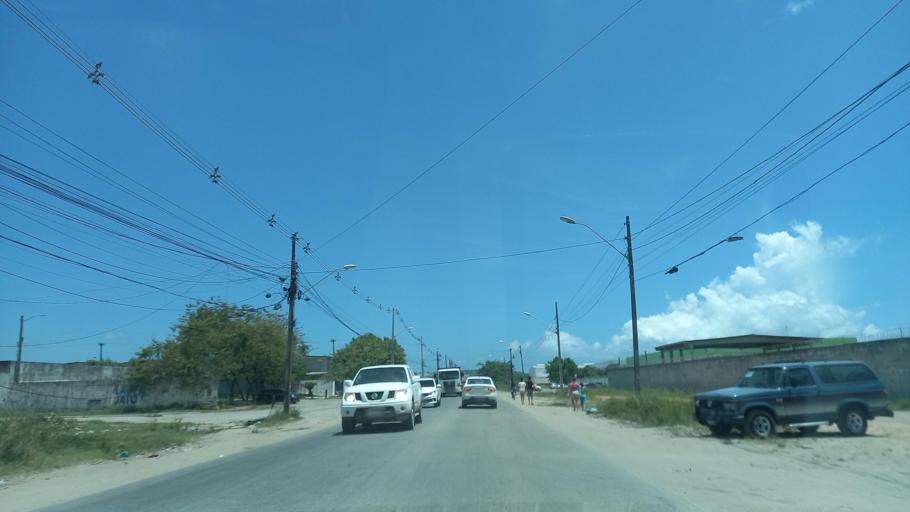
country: BR
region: Pernambuco
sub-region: Jaboatao Dos Guararapes
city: Jaboatao
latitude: -8.1563
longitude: -34.9667
